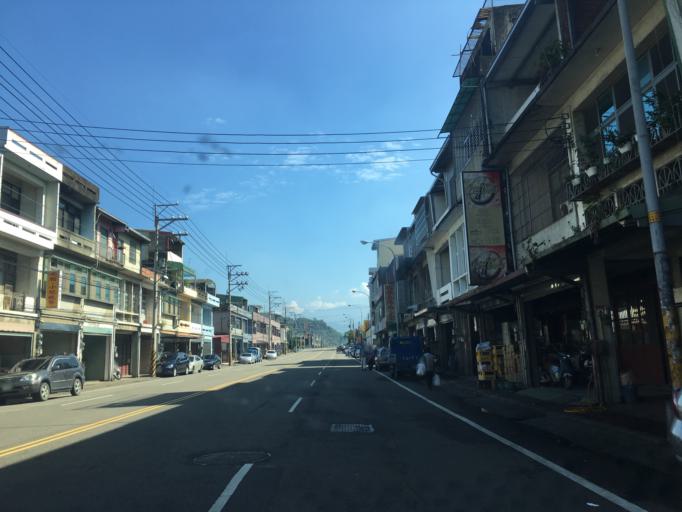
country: TW
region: Taiwan
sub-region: Hsinchu
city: Zhubei
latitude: 24.8122
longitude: 121.1309
